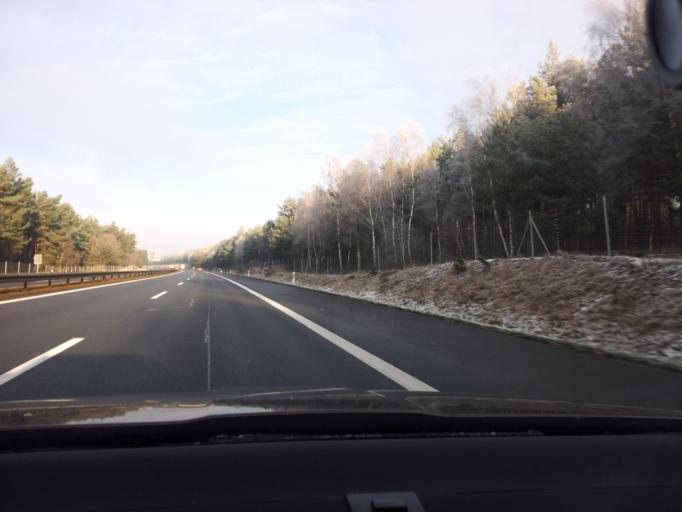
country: DE
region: Brandenburg
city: Wittstock
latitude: 53.0819
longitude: 12.5217
